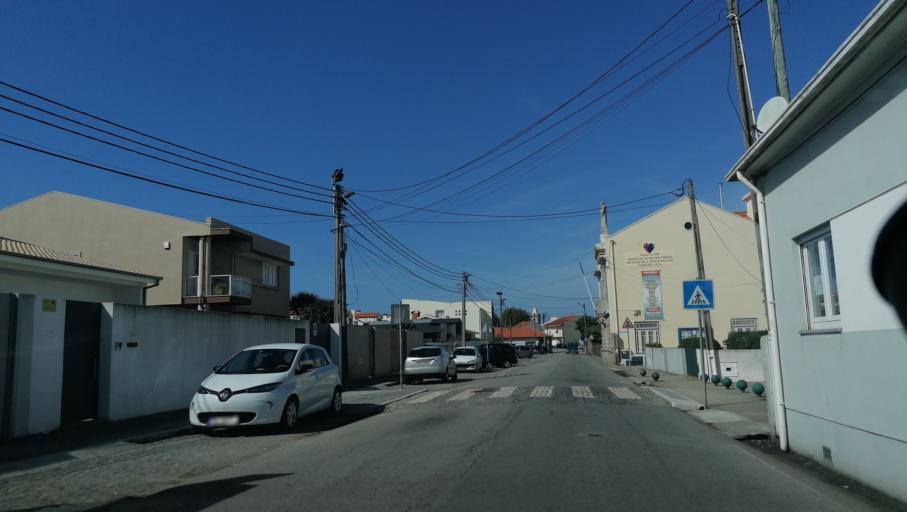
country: PT
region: Aveiro
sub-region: Espinho
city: Silvalde
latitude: 41.0042
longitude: -8.6231
